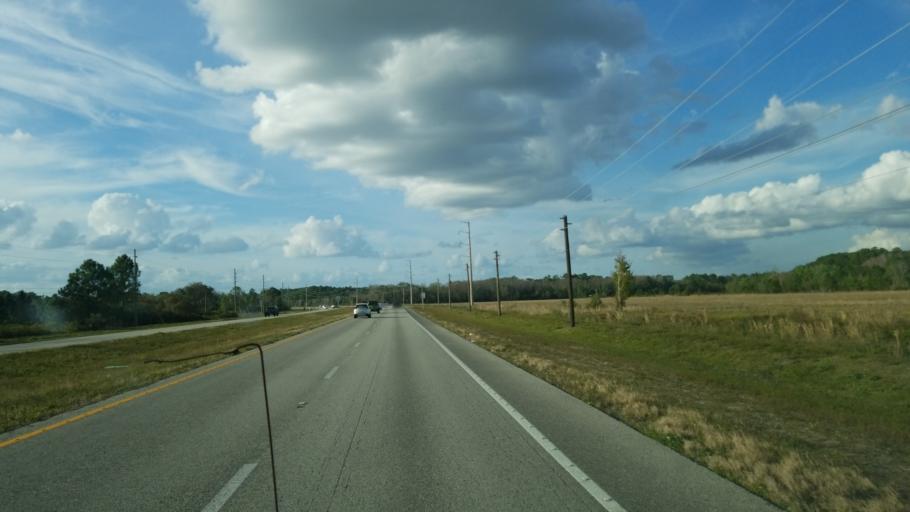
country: US
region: Florida
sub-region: Osceola County
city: Saint Cloud
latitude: 28.1771
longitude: -81.1329
